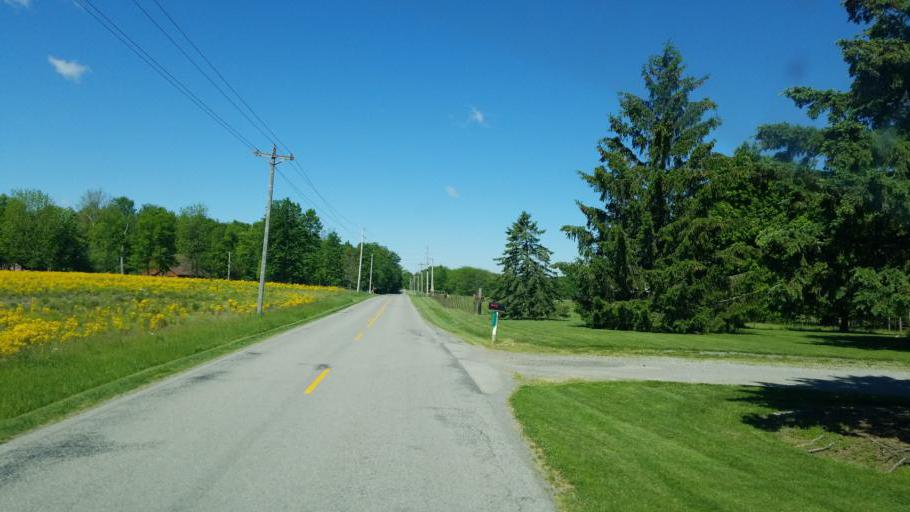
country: US
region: Ohio
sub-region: Logan County
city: Northwood
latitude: 40.4430
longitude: -83.6673
